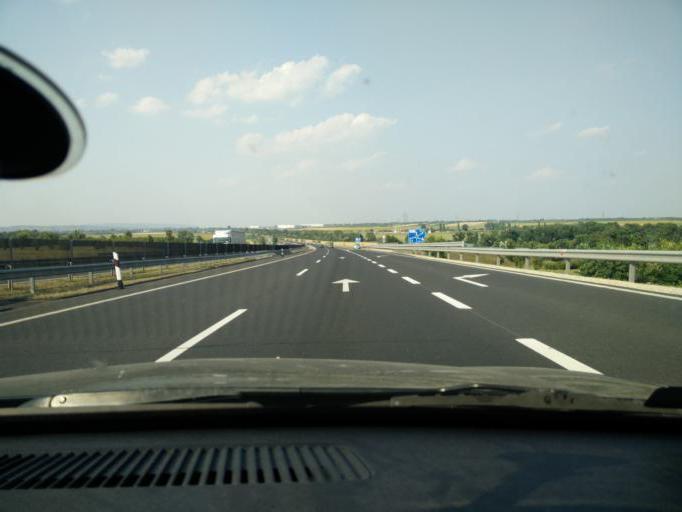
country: HU
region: Pest
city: Szazhalombatta
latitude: 47.3359
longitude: 18.8920
